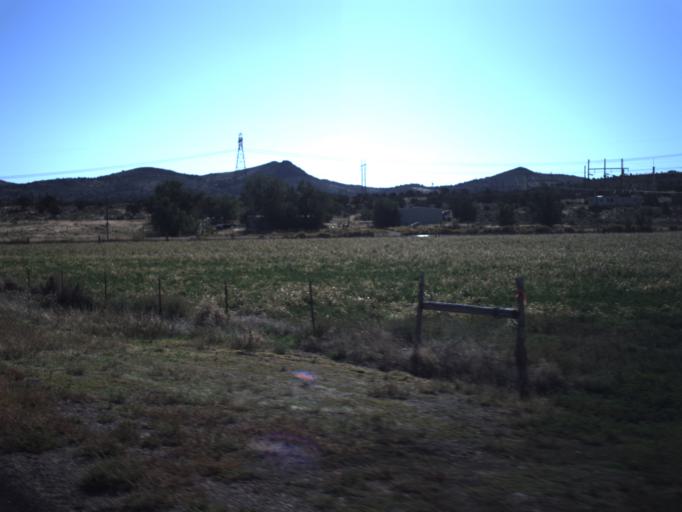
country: US
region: Utah
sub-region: Washington County
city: Enterprise
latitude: 37.6733
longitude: -113.5362
